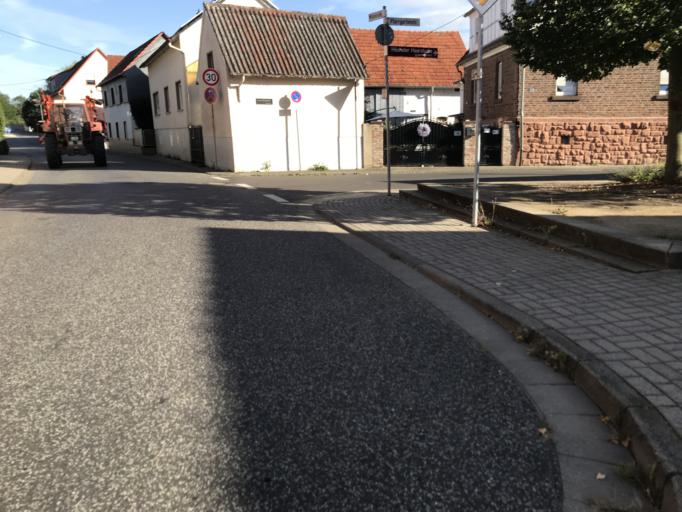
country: DE
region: Hesse
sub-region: Regierungsbezirk Darmstadt
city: Altenstadt
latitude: 50.2675
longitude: 8.9329
